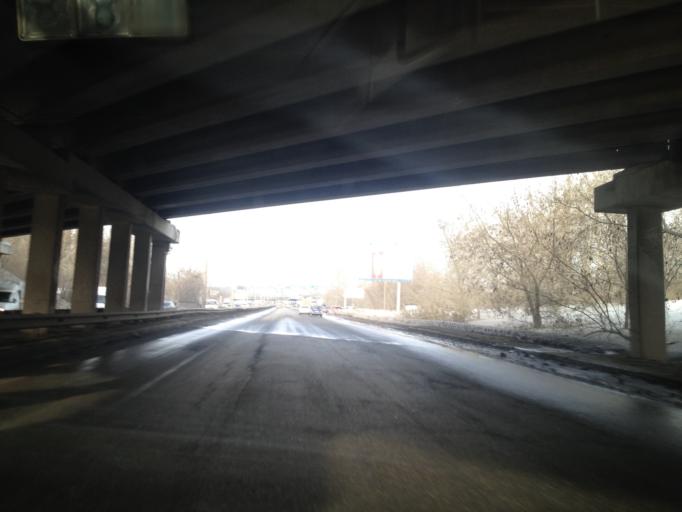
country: RU
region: Sverdlovsk
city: Yekaterinburg
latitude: 56.7951
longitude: 60.6403
